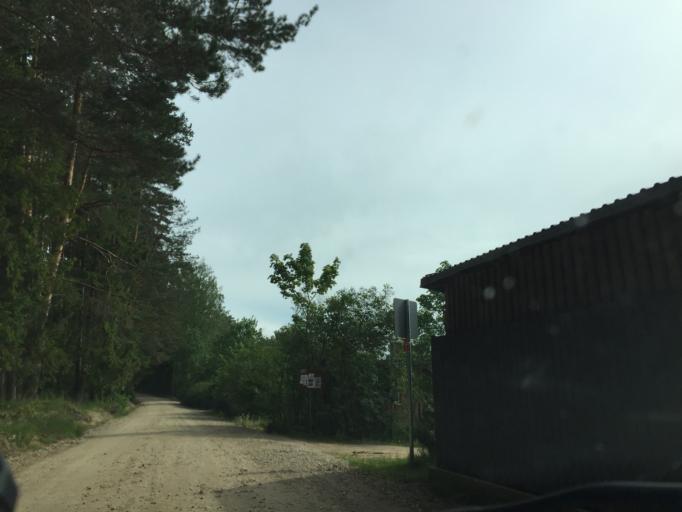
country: LV
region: Valmieras Rajons
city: Valmiera
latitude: 57.4775
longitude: 25.3979
